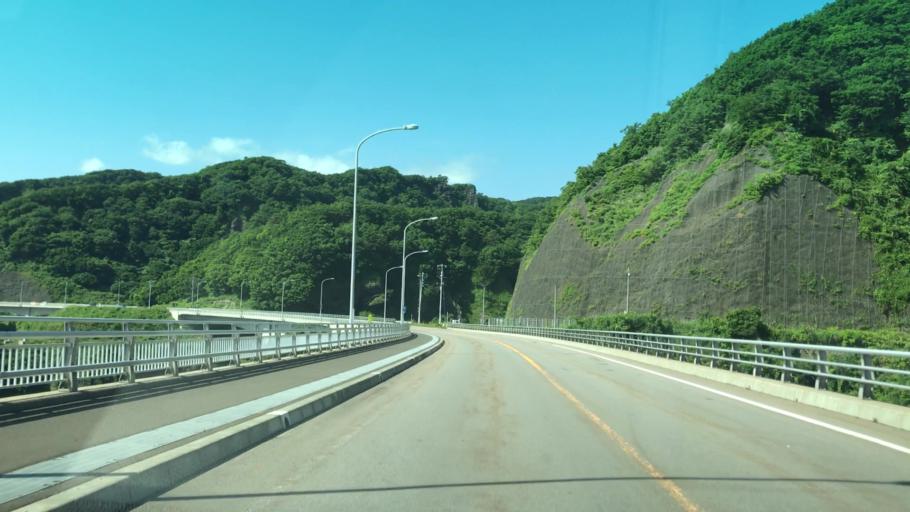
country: JP
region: Hokkaido
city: Iwanai
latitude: 43.1253
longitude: 140.4428
